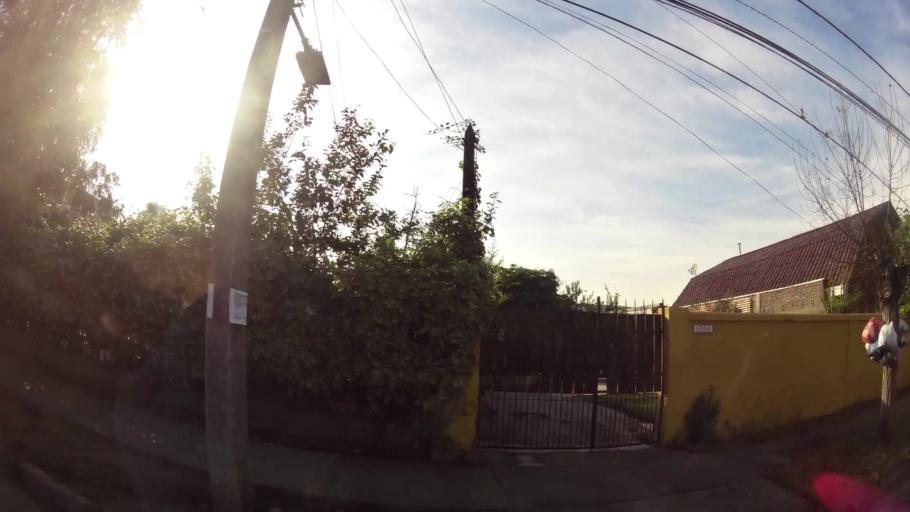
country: CL
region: Santiago Metropolitan
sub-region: Provincia de Santiago
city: Santiago
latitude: -33.5133
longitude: -70.6692
